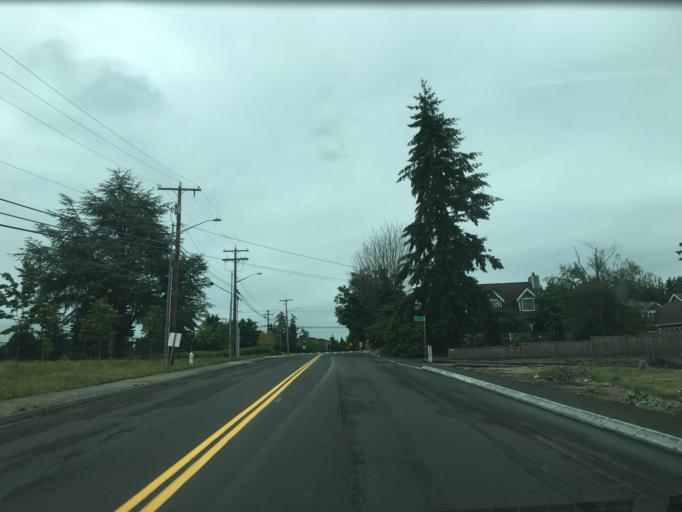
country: US
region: Washington
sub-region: King County
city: Inglewood-Finn Hill
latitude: 47.7152
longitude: -122.2314
